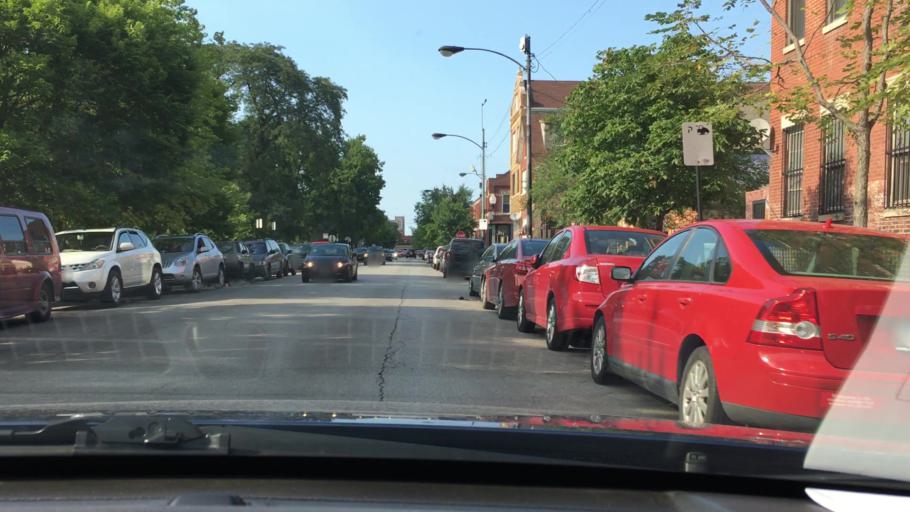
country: US
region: Illinois
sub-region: Cook County
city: Chicago
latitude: 41.8562
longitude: -87.6710
